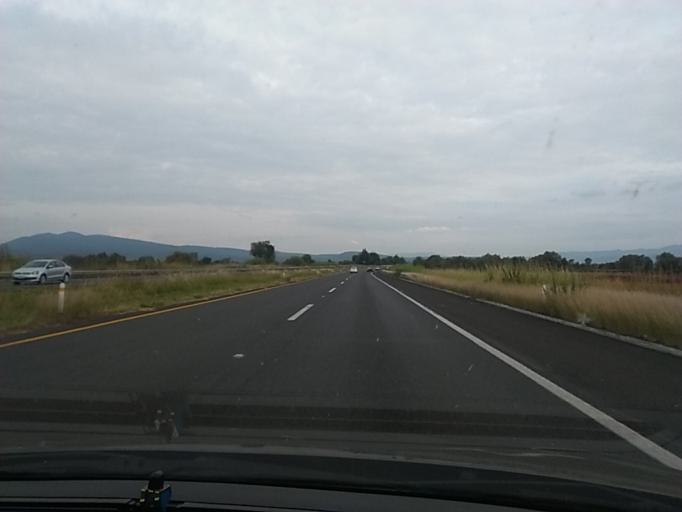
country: MX
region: Michoacan
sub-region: Jimenez
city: Copandaro (Copandaro del Cuatro)
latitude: 19.9379
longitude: -101.6204
